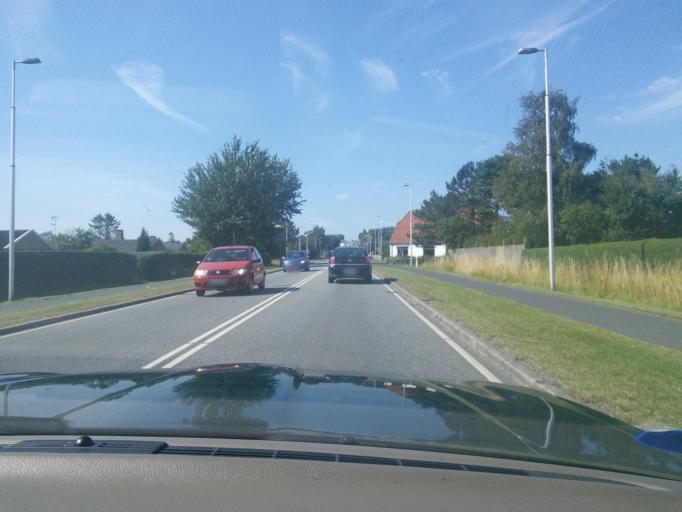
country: DK
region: Capital Region
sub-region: Halsnaes Kommune
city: Frederiksvaerk
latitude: 55.9502
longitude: 12.0437
